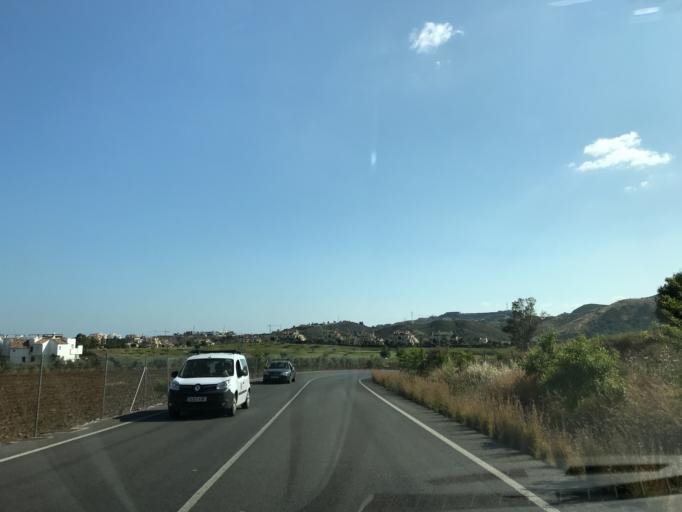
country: ES
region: Andalusia
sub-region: Provincia de Malaga
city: Benahavis
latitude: 36.5073
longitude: -5.0187
